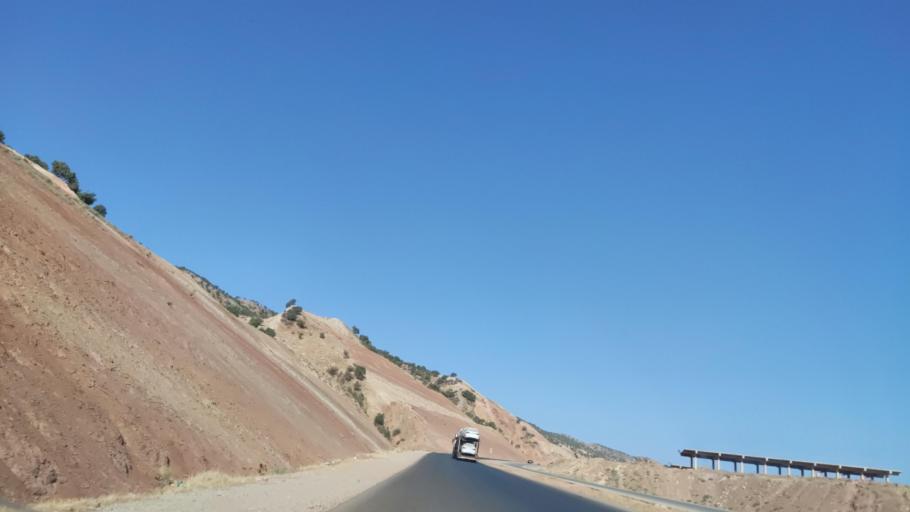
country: IQ
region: Arbil
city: Shaqlawah
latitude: 36.4329
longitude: 44.3056
